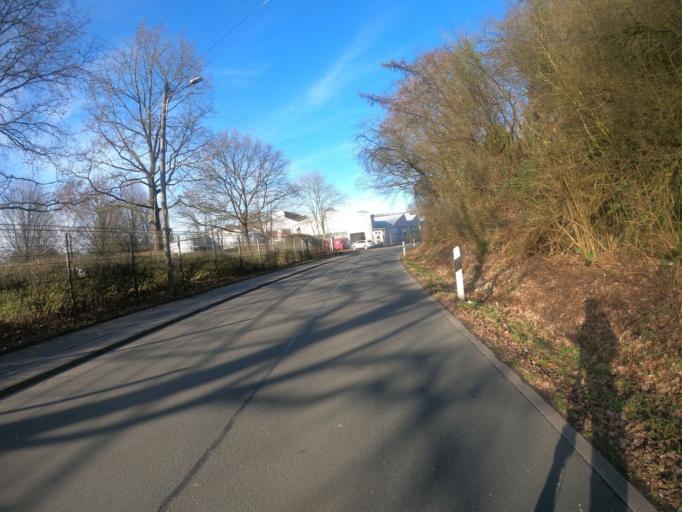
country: DE
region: North Rhine-Westphalia
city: Sprockhovel
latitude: 51.2921
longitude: 7.2332
